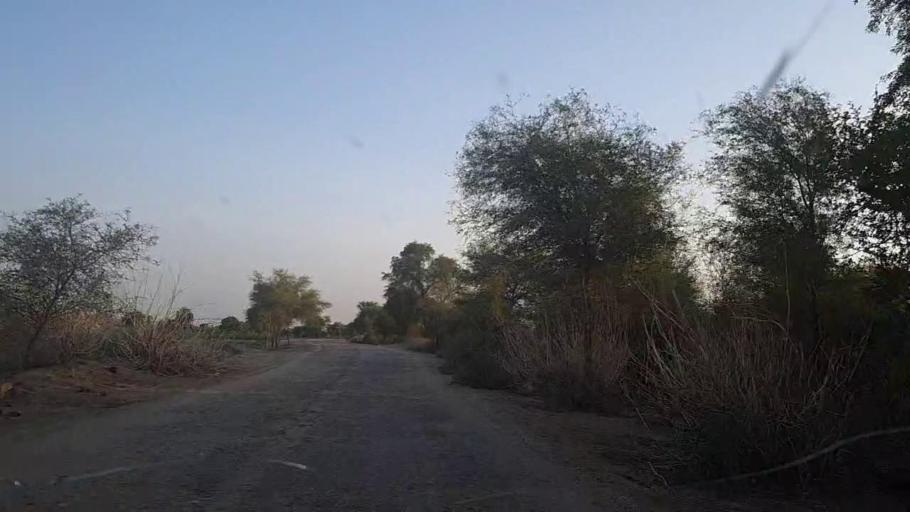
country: PK
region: Sindh
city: Khanpur
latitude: 27.6122
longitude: 69.4382
